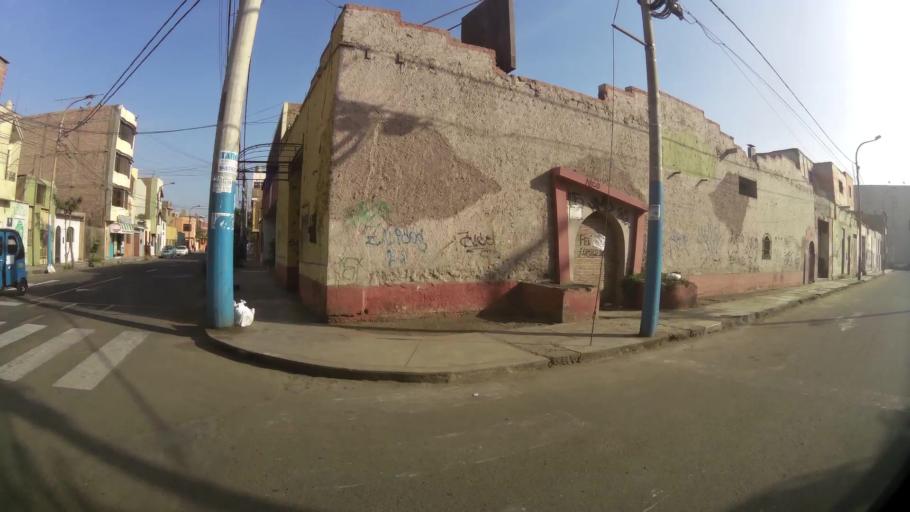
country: PE
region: Lima
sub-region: Huaura
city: Huacho
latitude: -11.1093
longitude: -77.6124
